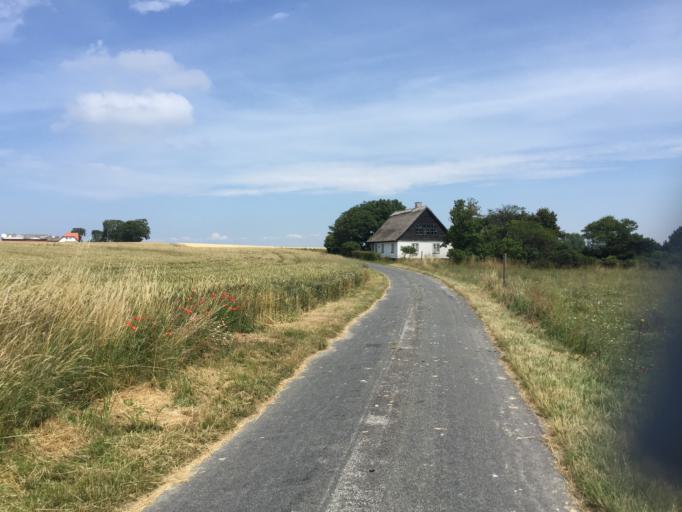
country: DK
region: Zealand
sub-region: Slagelse Kommune
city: Skaelskor
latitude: 55.1991
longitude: 11.1860
